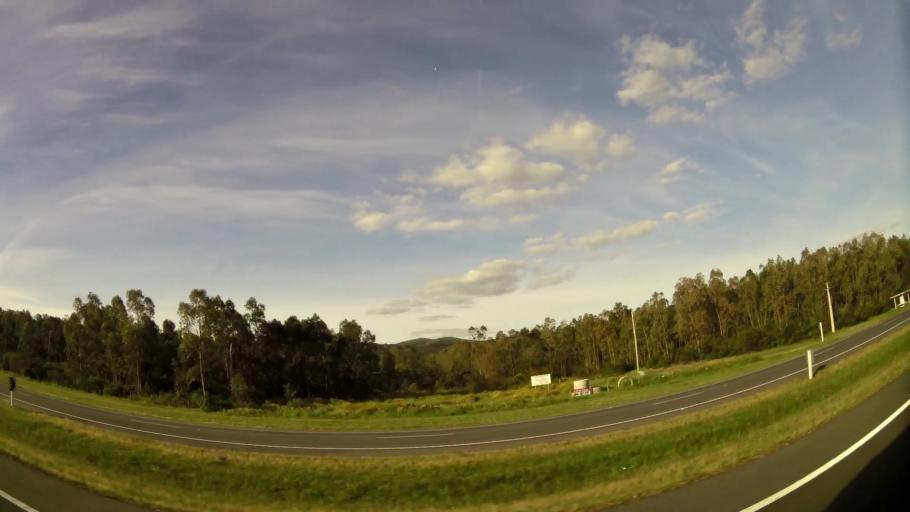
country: UY
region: Maldonado
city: Piriapolis
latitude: -34.7861
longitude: -55.3336
